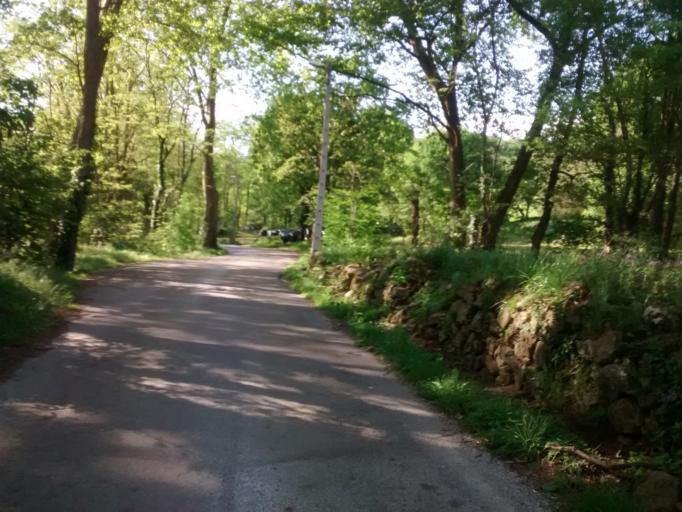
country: ES
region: Cantabria
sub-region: Provincia de Cantabria
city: Entrambasaguas
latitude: 43.3370
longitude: -3.6595
